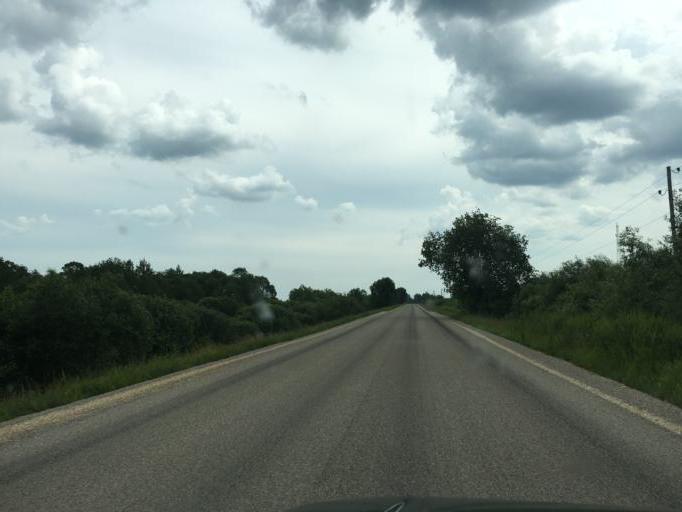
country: LV
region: Rugaju
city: Rugaji
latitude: 56.8528
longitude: 27.0877
